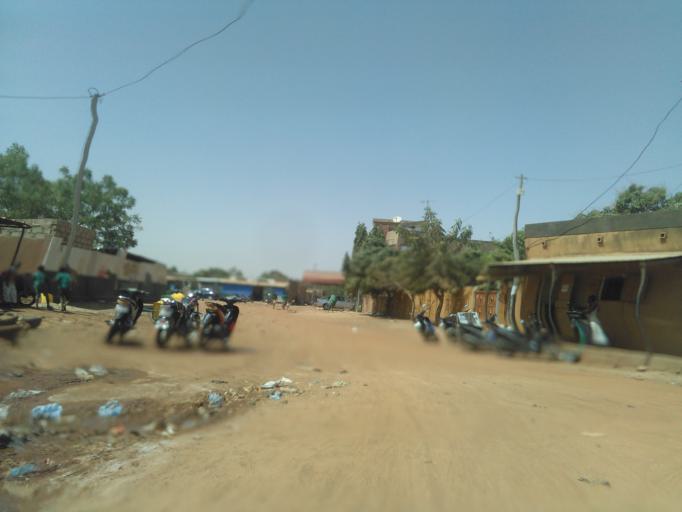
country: BF
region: Centre
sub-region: Kadiogo Province
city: Ouagadougou
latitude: 12.3942
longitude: -1.5716
